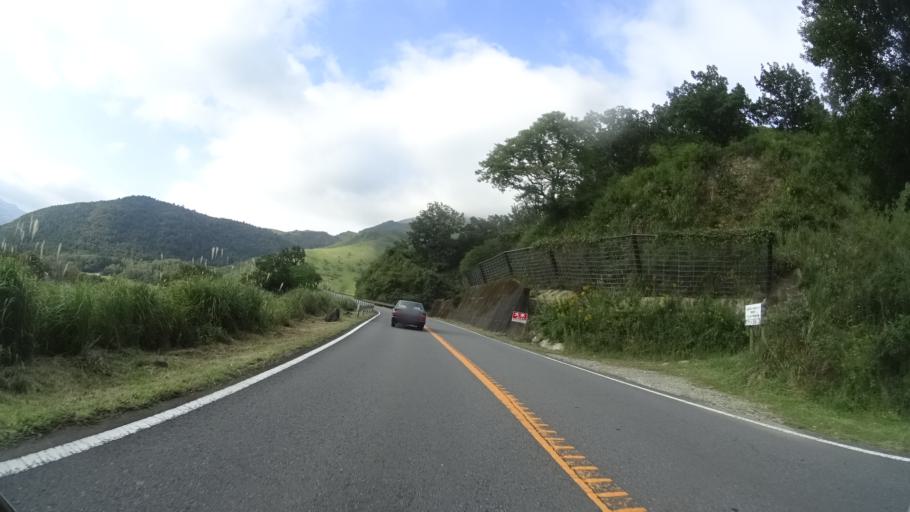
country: JP
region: Oita
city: Beppu
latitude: 33.2588
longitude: 131.3812
